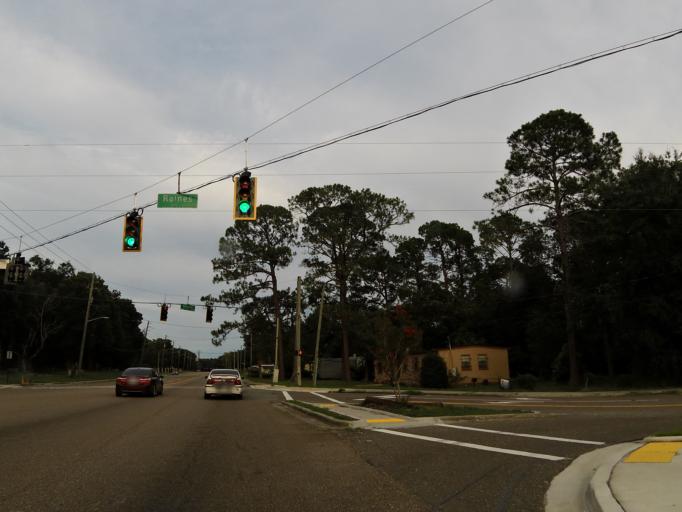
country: US
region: Florida
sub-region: Duval County
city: Jacksonville
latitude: 30.3832
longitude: -81.7059
